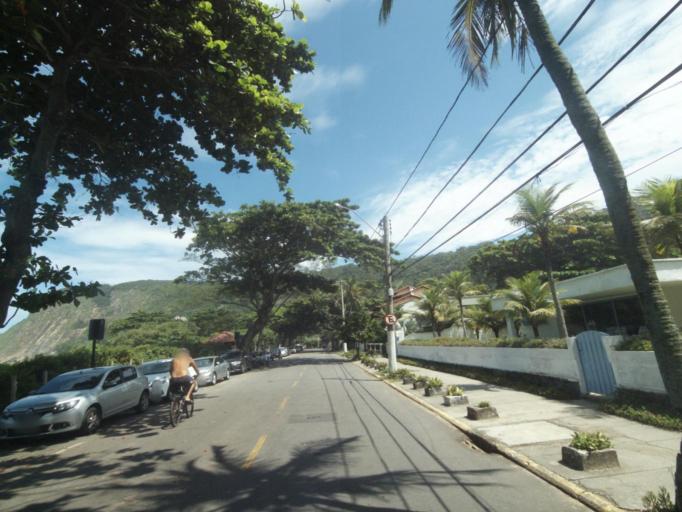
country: BR
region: Rio de Janeiro
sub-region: Niteroi
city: Niteroi
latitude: -22.9736
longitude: -43.0355
